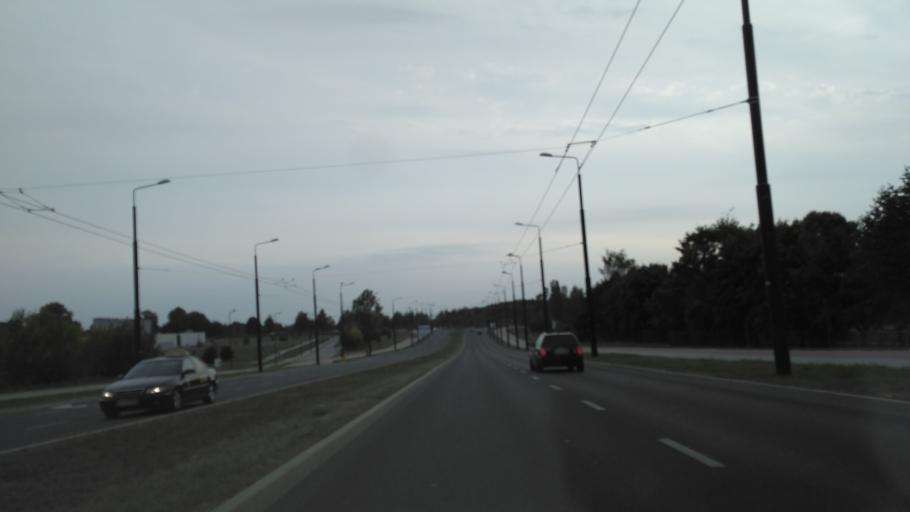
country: PL
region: Lublin Voivodeship
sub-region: Powiat lubelski
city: Jakubowice Murowane
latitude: 51.2266
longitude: 22.6174
